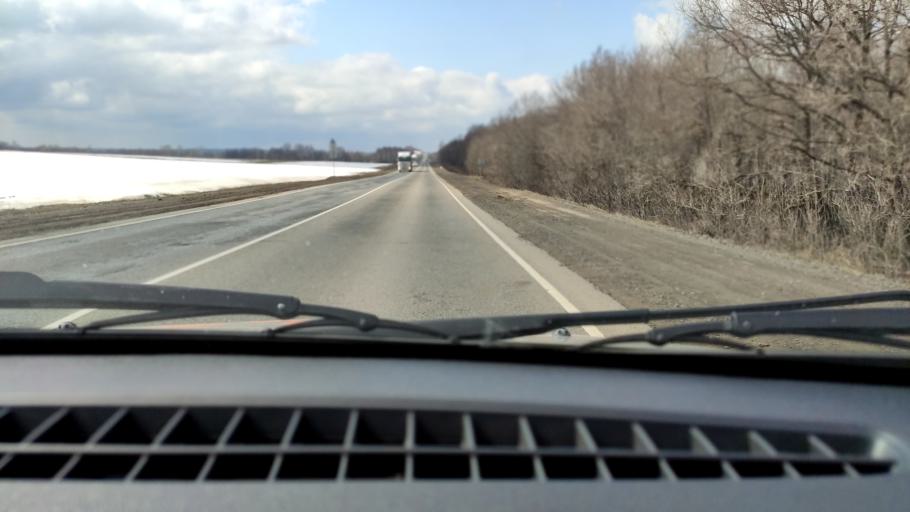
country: RU
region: Bashkortostan
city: Kudeyevskiy
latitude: 54.8028
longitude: 56.6150
